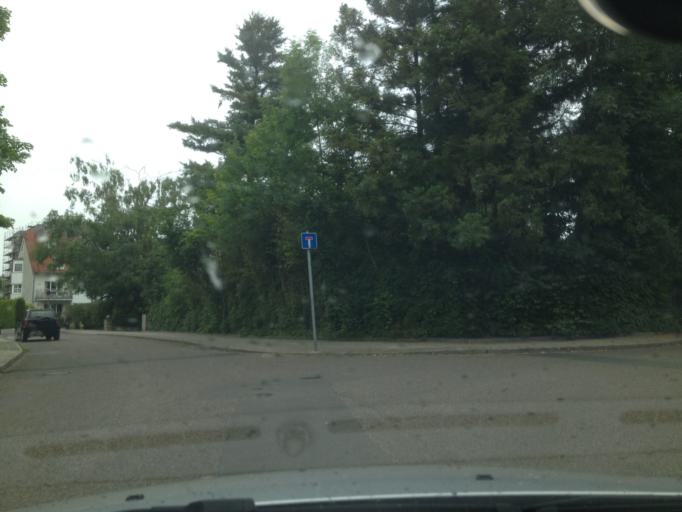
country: DE
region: North Rhine-Westphalia
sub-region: Regierungsbezirk Munster
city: Gelsenkirchen
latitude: 51.4321
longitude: 7.1118
